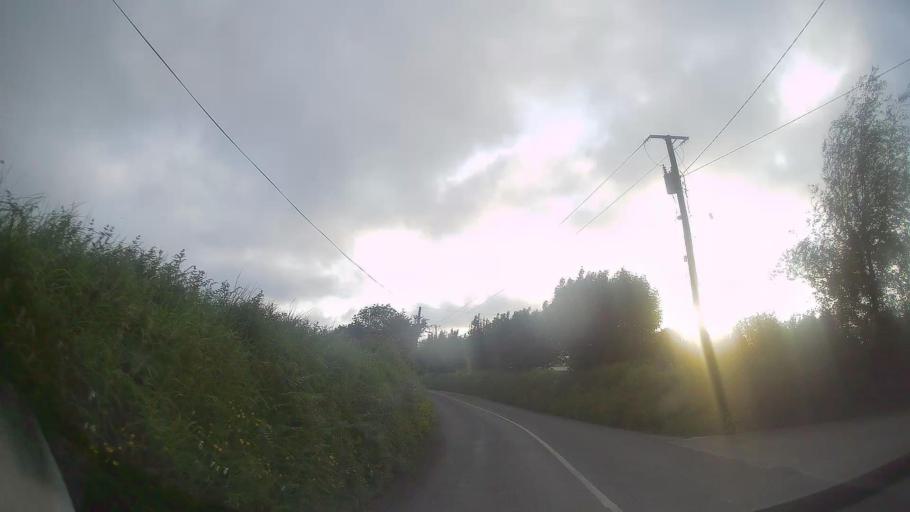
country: IE
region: Munster
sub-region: County Cork
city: Blarney
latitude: 51.9786
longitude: -8.5429
